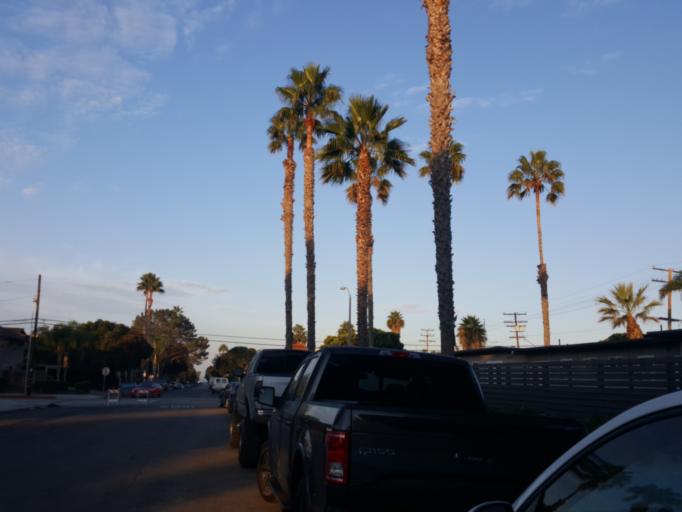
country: US
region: California
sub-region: San Diego County
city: La Jolla
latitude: 32.7978
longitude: -117.2455
